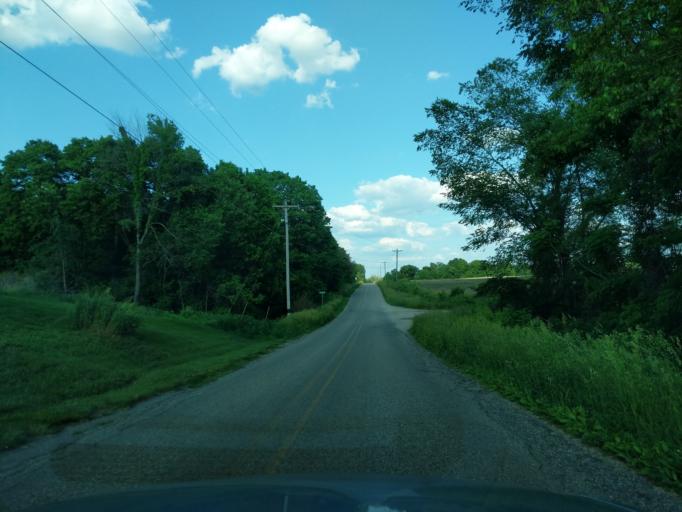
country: US
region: Indiana
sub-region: Kosciusko County
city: North Webster
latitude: 41.3025
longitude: -85.6000
